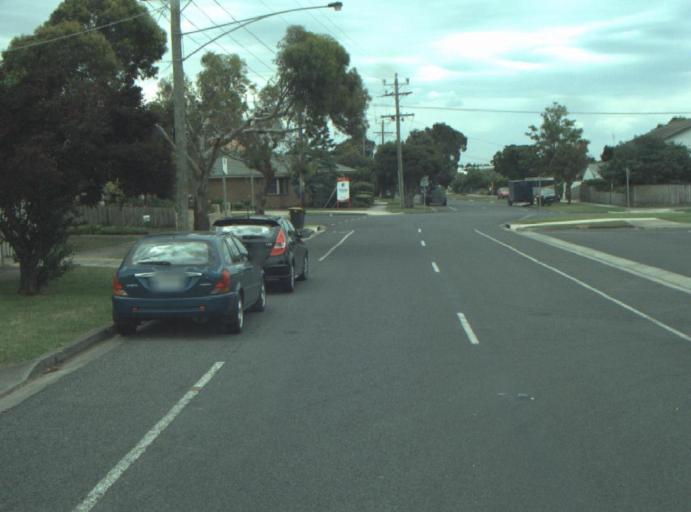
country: AU
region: Victoria
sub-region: Greater Geelong
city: Leopold
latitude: -38.1872
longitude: 144.4701
